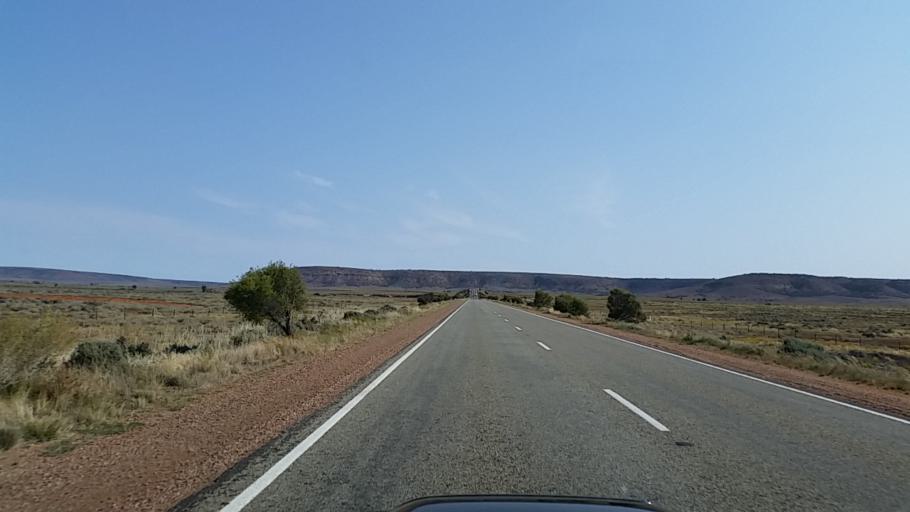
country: AU
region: South Australia
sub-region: Port Augusta
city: Port Augusta West
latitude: -32.5357
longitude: 137.6512
